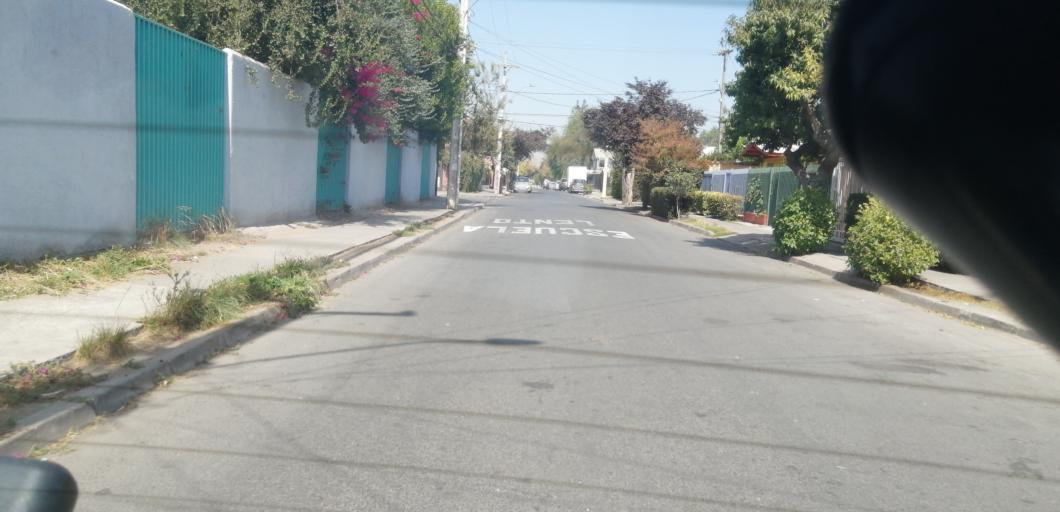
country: CL
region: Santiago Metropolitan
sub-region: Provincia de Santiago
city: Lo Prado
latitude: -33.4648
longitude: -70.7430
